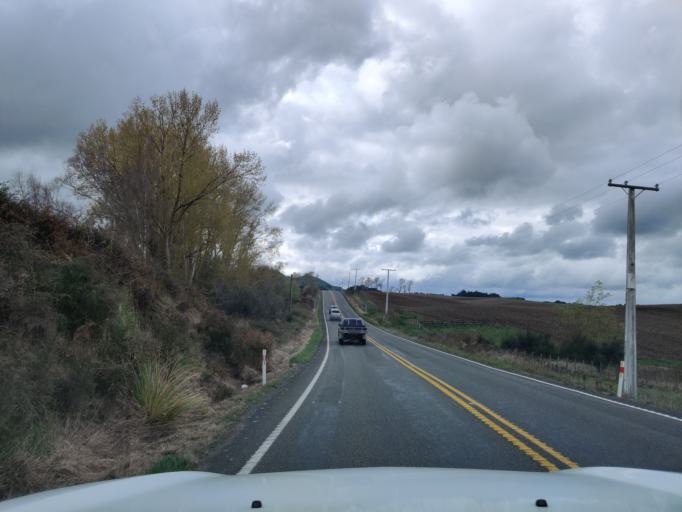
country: NZ
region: Manawatu-Wanganui
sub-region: Ruapehu District
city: Waiouru
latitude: -39.4809
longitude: 175.3016
